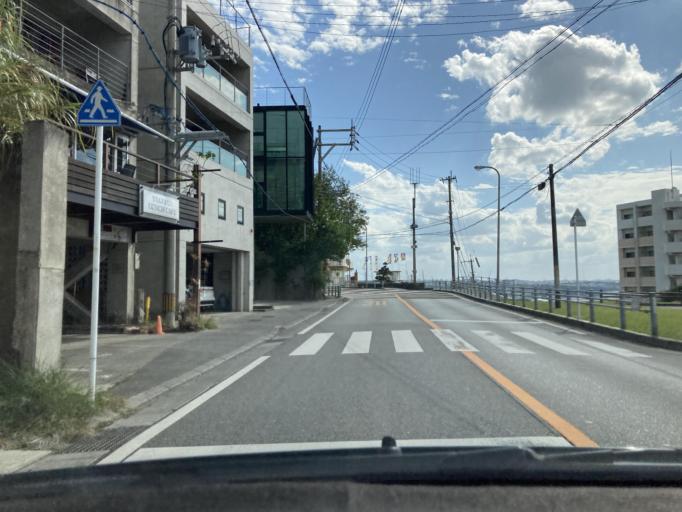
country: JP
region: Okinawa
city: Chatan
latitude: 26.3174
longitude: 127.7726
